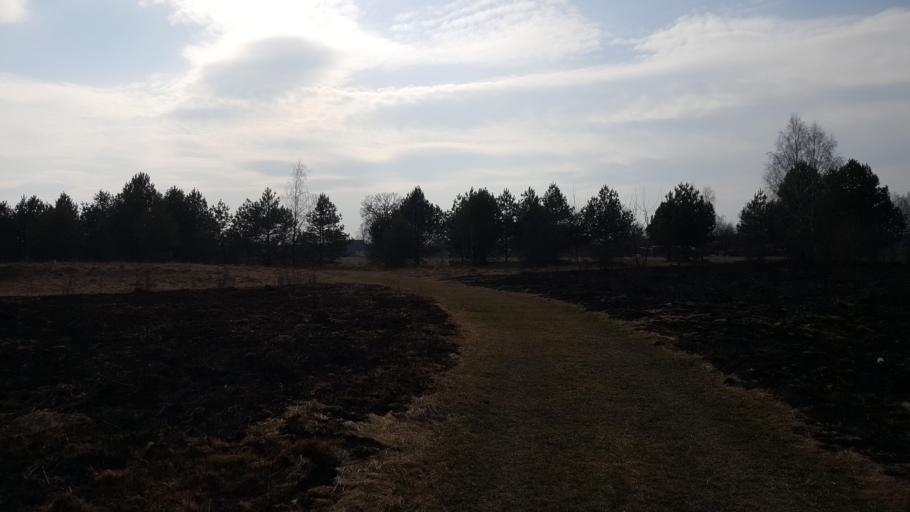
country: BY
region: Brest
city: Kamyanyets
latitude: 52.3152
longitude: 23.9246
